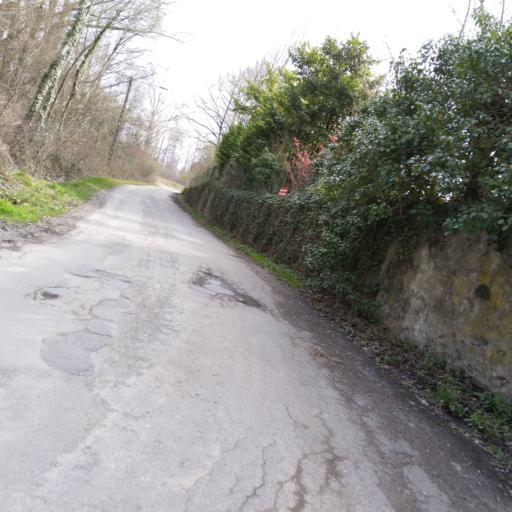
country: BE
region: Wallonia
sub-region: Province du Hainaut
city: Soignies
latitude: 50.5707
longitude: 4.0537
